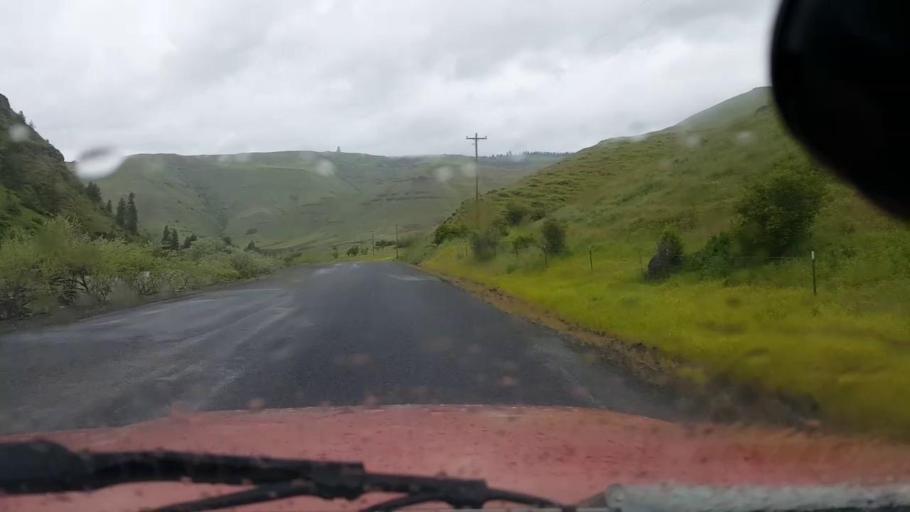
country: US
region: Washington
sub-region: Asotin County
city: Asotin
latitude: 46.0361
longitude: -117.2785
